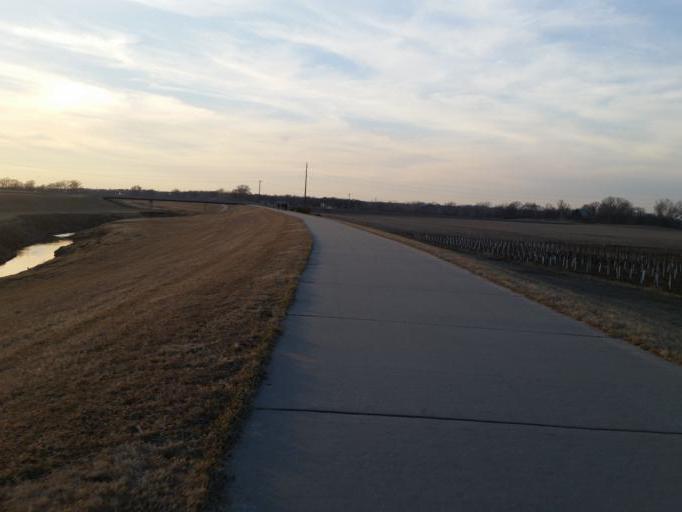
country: US
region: Nebraska
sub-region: Sarpy County
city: Papillion
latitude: 41.1479
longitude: -95.9813
